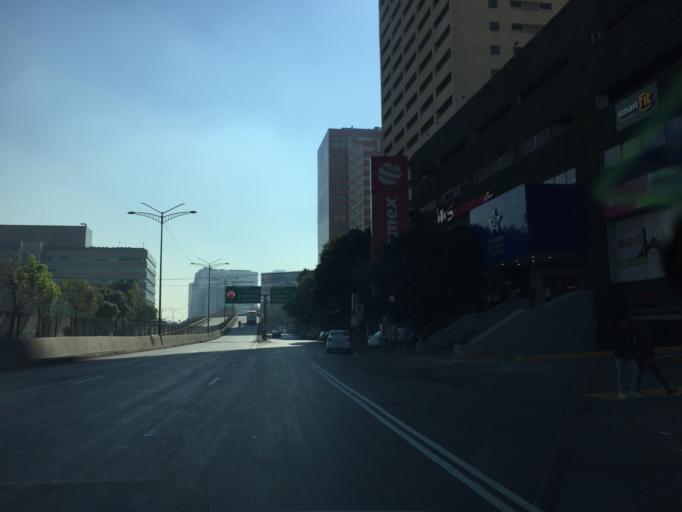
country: MX
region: Mexico City
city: Cuauhtemoc
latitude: 19.4375
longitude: -99.1720
